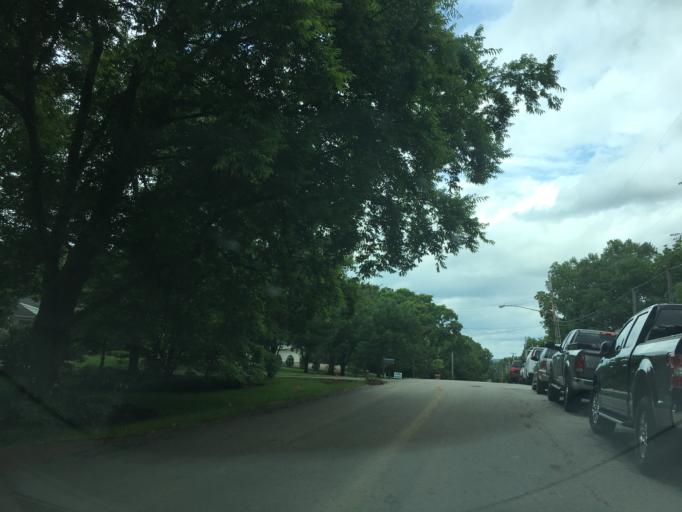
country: US
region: Tennessee
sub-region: Davidson County
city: Belle Meade
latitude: 36.0948
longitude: -86.8349
